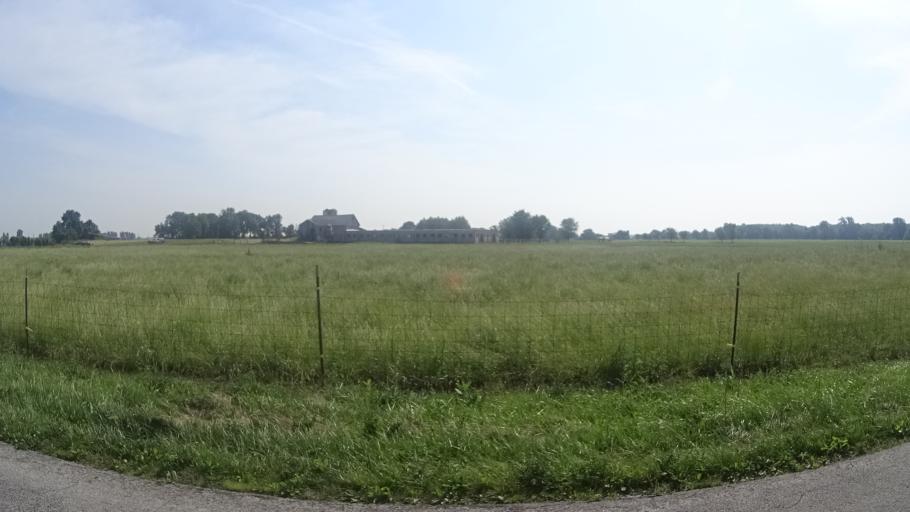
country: US
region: Ohio
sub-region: Huron County
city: Bellevue
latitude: 41.2901
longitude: -82.7703
